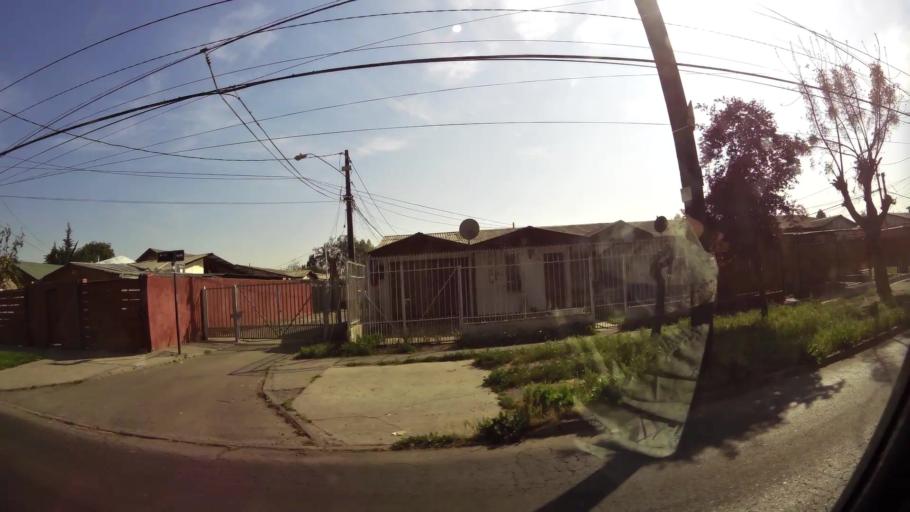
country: CL
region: Santiago Metropolitan
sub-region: Provincia de Santiago
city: Lo Prado
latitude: -33.4673
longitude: -70.7428
